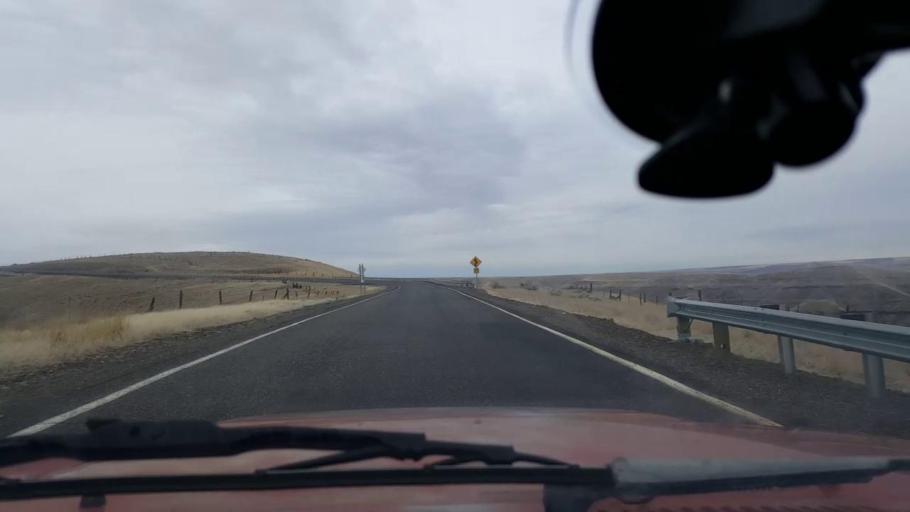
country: US
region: Washington
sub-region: Asotin County
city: Clarkston Heights-Vineland
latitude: 46.3335
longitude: -117.2981
